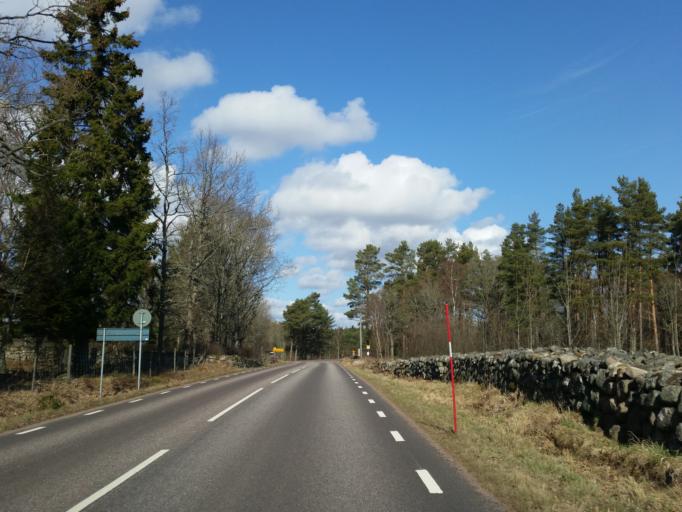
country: SE
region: Kalmar
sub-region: Monsteras Kommun
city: Timmernabben
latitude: 56.8765
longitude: 16.4319
